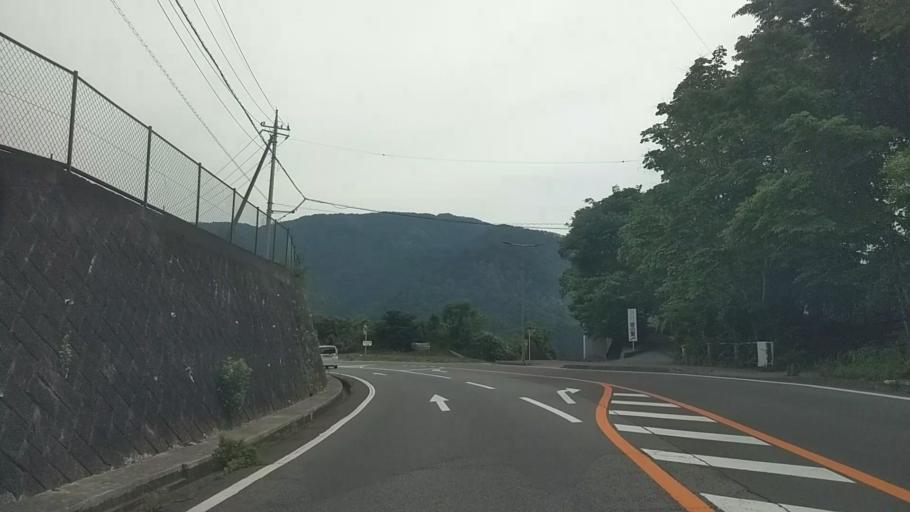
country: JP
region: Yamanashi
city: Isawa
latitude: 35.5737
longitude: 138.5905
